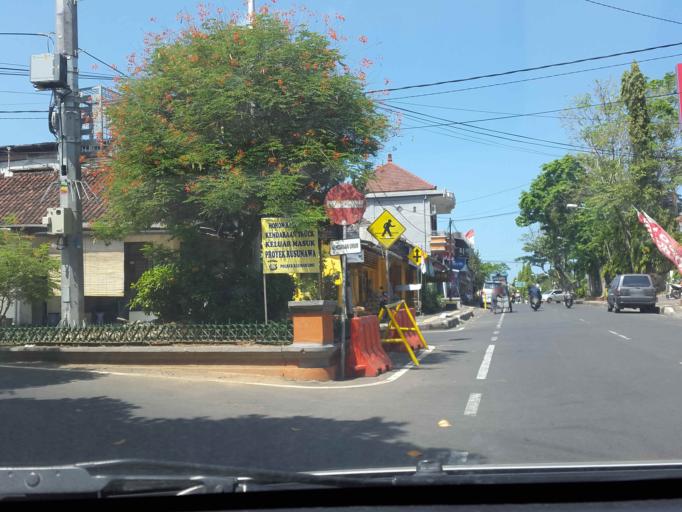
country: ID
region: Bali
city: Klungkung
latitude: -8.5348
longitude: 115.4003
